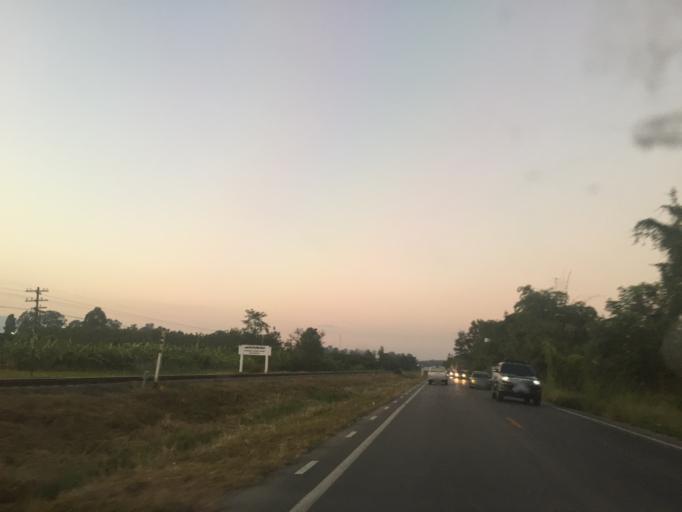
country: TH
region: Chiang Mai
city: Saraphi
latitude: 18.6661
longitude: 99.0446
